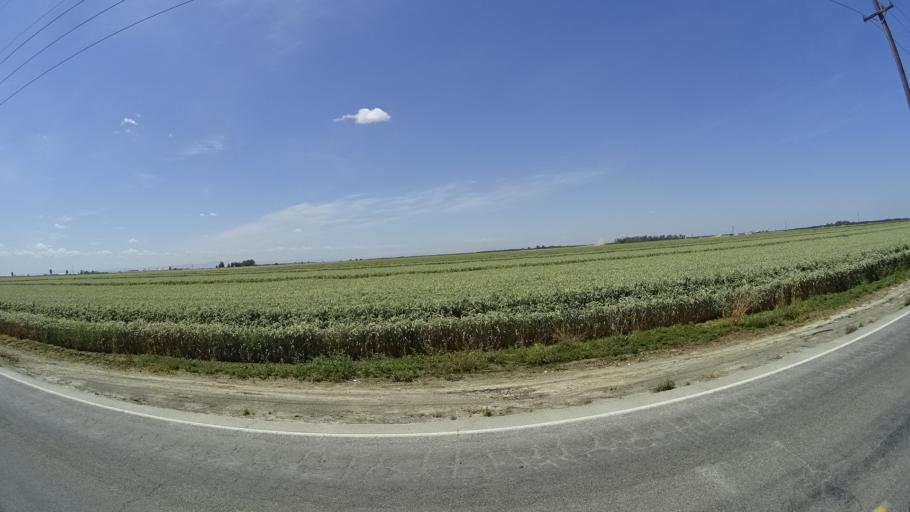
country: US
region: California
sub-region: Kings County
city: Home Garden
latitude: 36.2449
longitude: -119.6549
